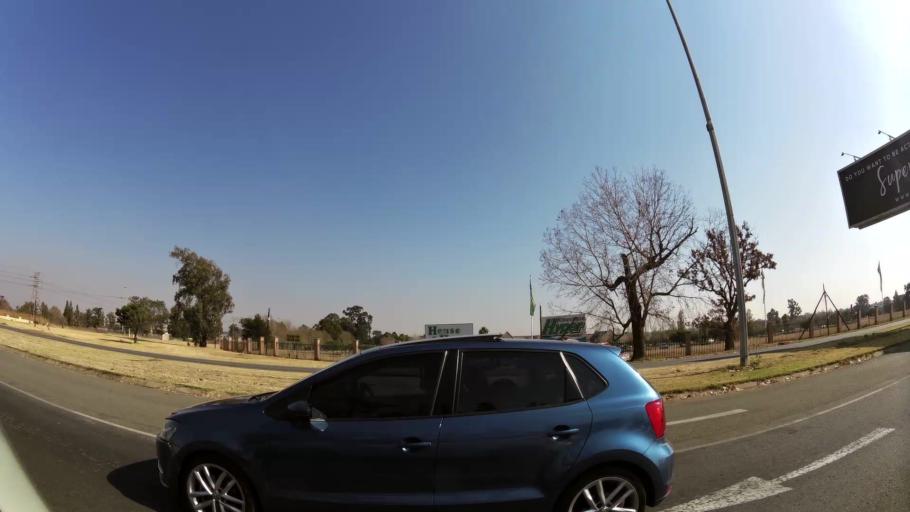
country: ZA
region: Gauteng
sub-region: Ekurhuleni Metropolitan Municipality
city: Boksburg
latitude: -26.2284
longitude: 28.2492
